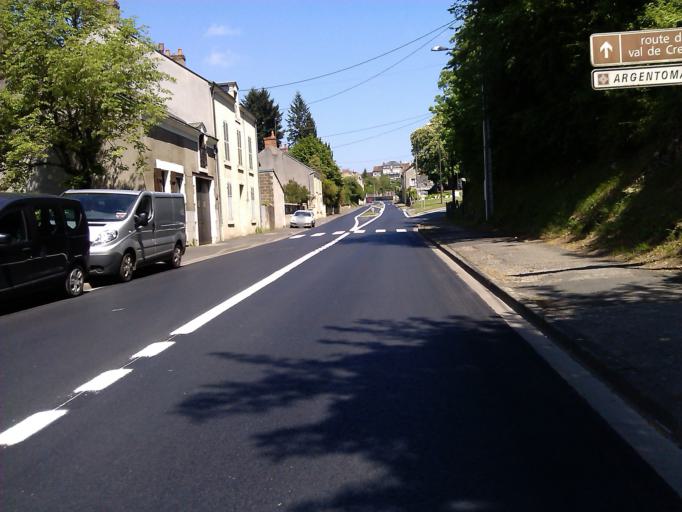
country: FR
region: Centre
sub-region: Departement de l'Indre
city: Saint-Marcel
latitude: 46.5975
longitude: 1.5115
